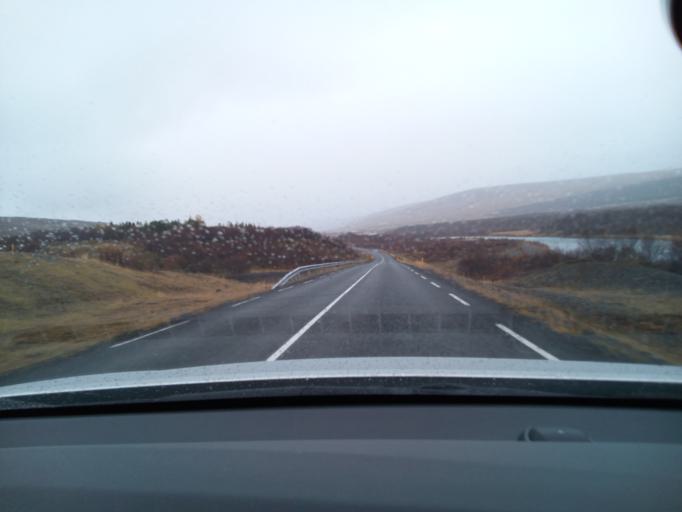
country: IS
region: South
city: Hveragerdi
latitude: 64.7019
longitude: -20.9878
